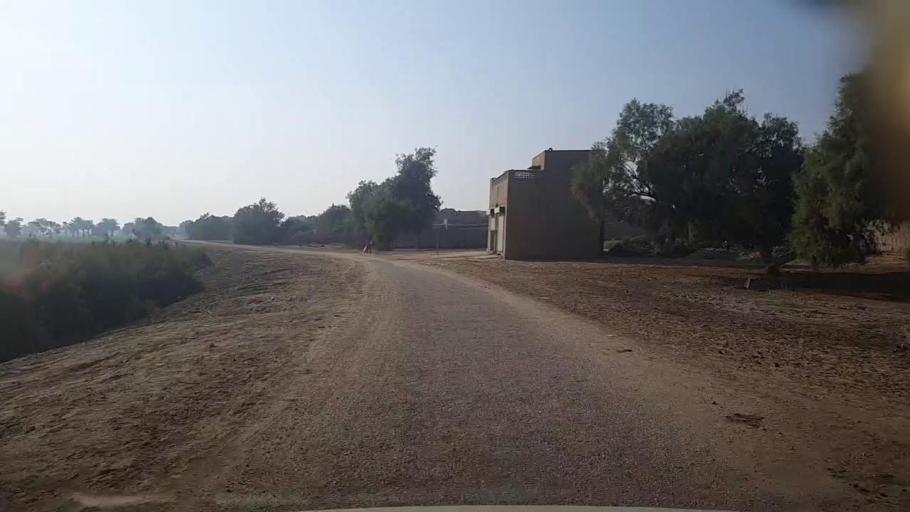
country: PK
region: Sindh
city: Karaundi
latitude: 26.7888
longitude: 68.4737
